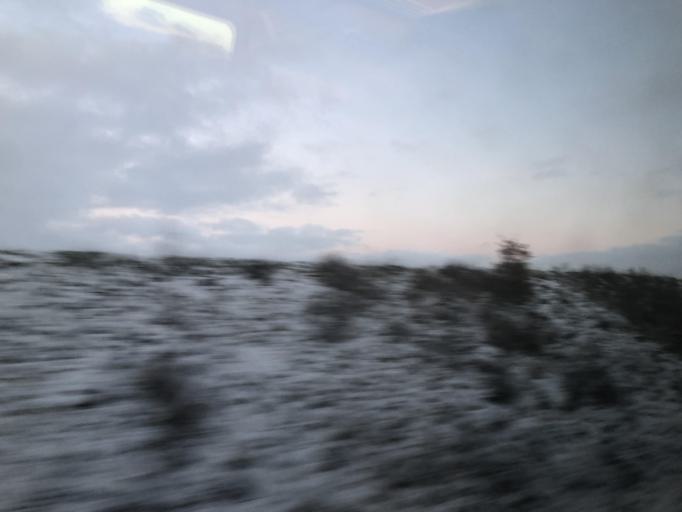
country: SE
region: Skane
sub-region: Kavlinge Kommun
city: Kaevlinge
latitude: 55.8123
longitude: 13.1049
